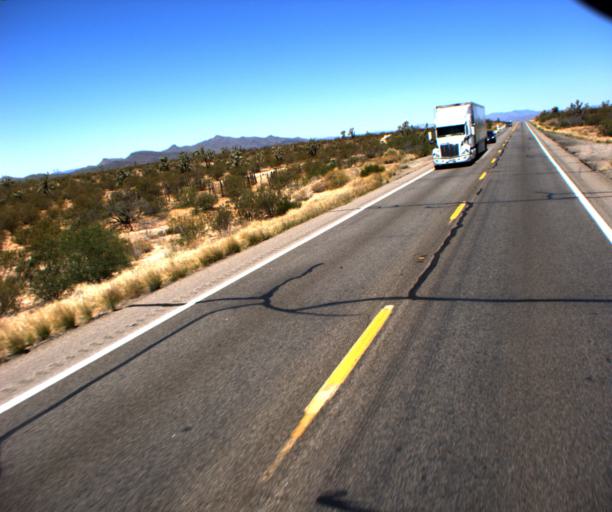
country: US
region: Arizona
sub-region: Yavapai County
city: Congress
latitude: 34.2430
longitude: -113.0775
